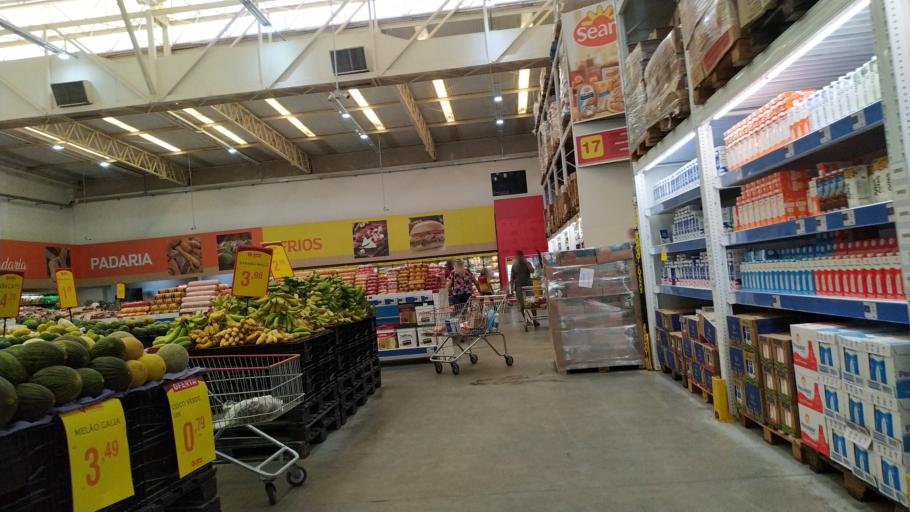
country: BR
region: Rio Grande do Norte
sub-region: Mossoro
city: Mossoro
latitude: -5.1905
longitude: -37.3356
